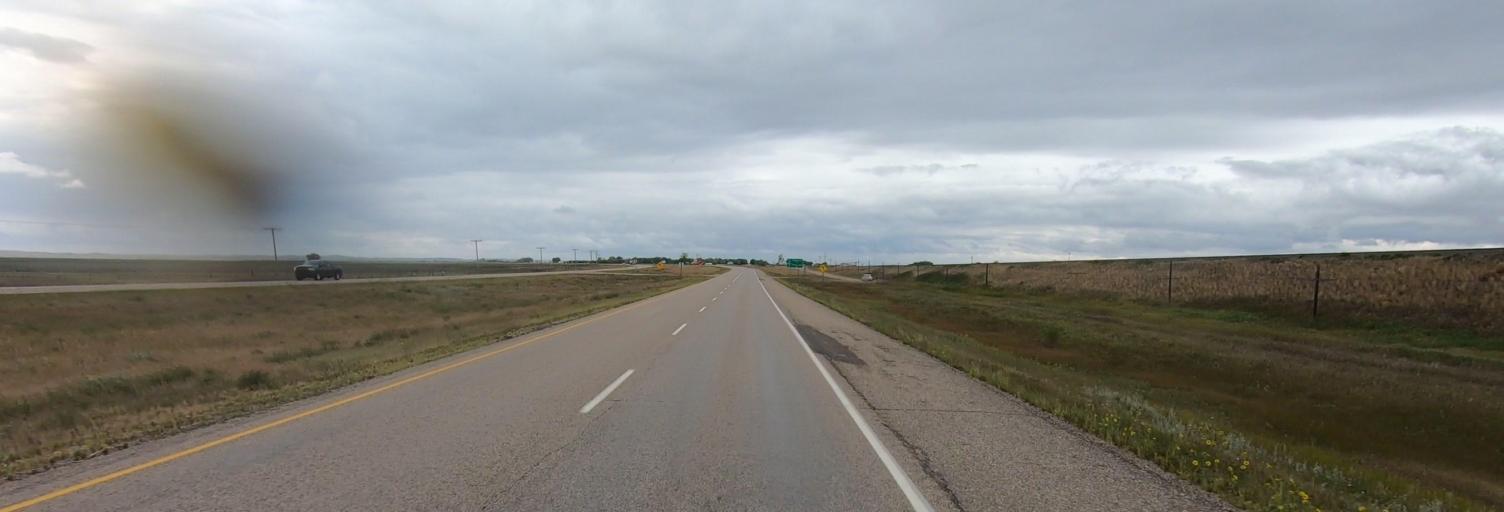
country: CA
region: Saskatchewan
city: Gravelbourg
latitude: 50.4639
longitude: -106.6212
